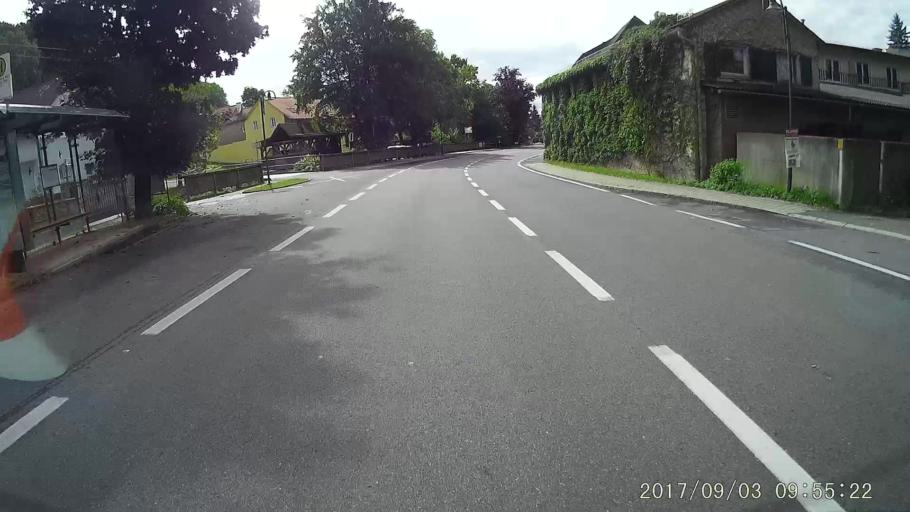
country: AT
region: Styria
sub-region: Politischer Bezirk Suedoststeiermark
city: Bad Gleichenberg
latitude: 46.8860
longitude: 15.8977
